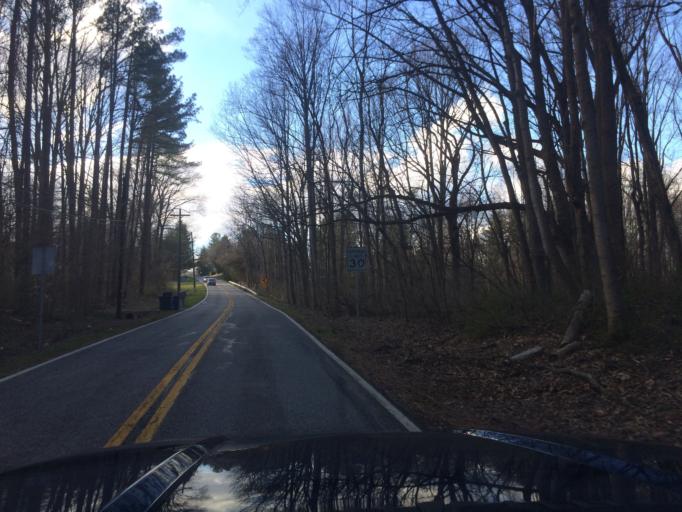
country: US
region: Maryland
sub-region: Carroll County
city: Eldersburg
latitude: 39.3892
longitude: -76.9113
